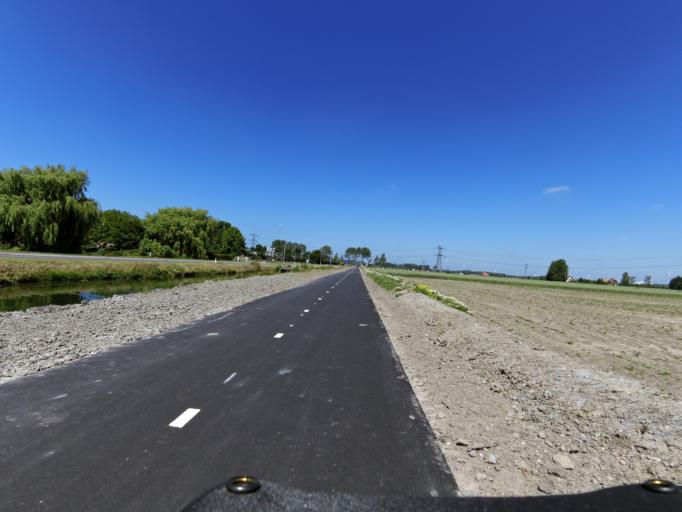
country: NL
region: South Holland
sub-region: Gemeente Brielle
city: Brielle
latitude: 51.9087
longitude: 4.1195
